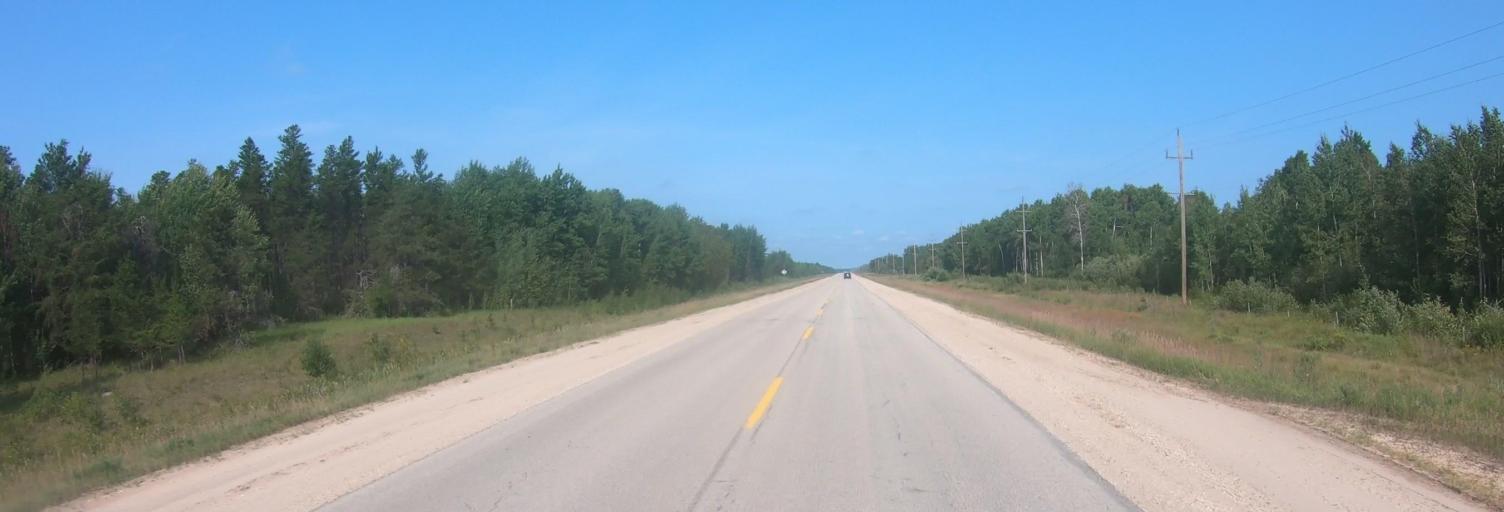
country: US
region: Minnesota
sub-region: Roseau County
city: Roseau
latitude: 49.1409
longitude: -96.1055
